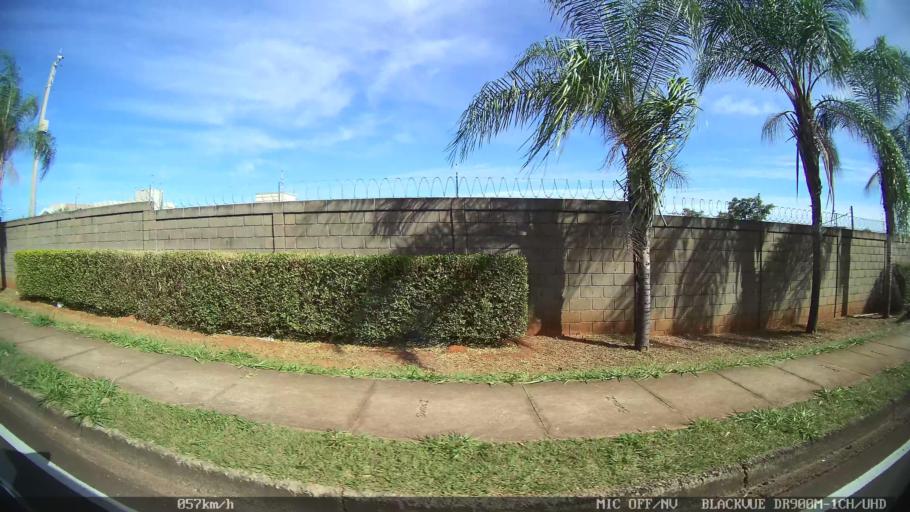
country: BR
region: Sao Paulo
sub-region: Sao Jose Do Rio Preto
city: Sao Jose do Rio Preto
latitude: -20.8105
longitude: -49.3383
